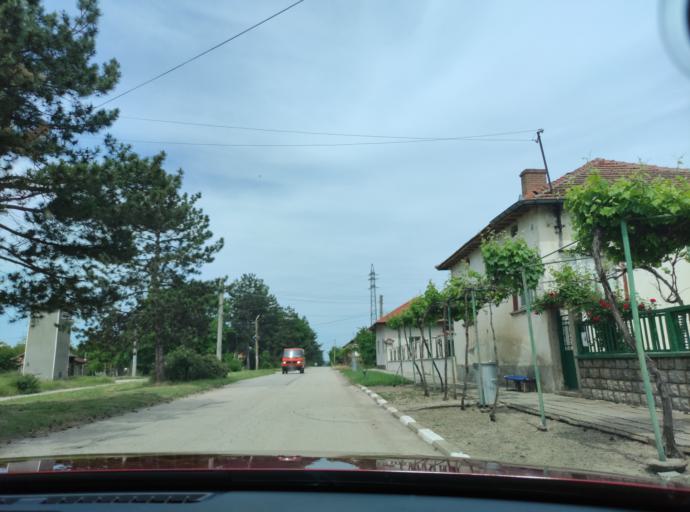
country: BG
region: Pleven
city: Iskur
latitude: 43.5364
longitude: 24.2860
